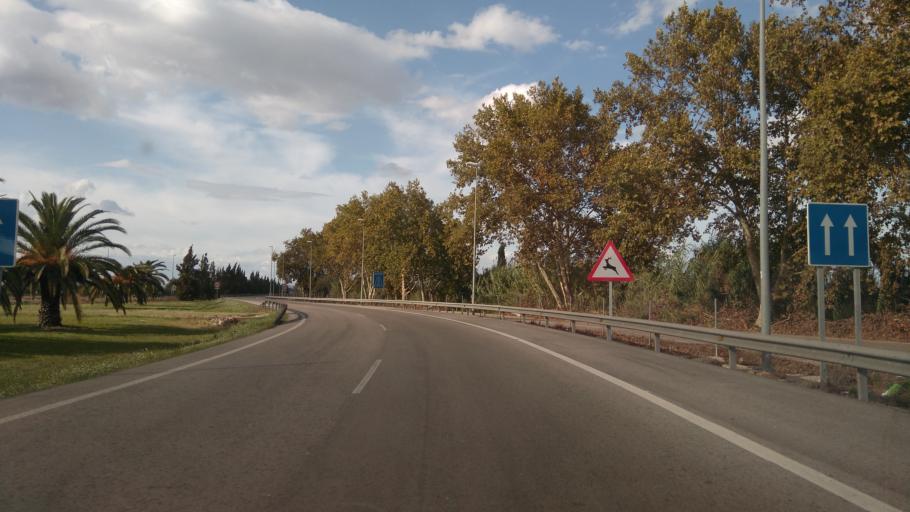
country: ES
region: Valencia
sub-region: Provincia de Valencia
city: Guadassuar
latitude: 39.1624
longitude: -0.4559
